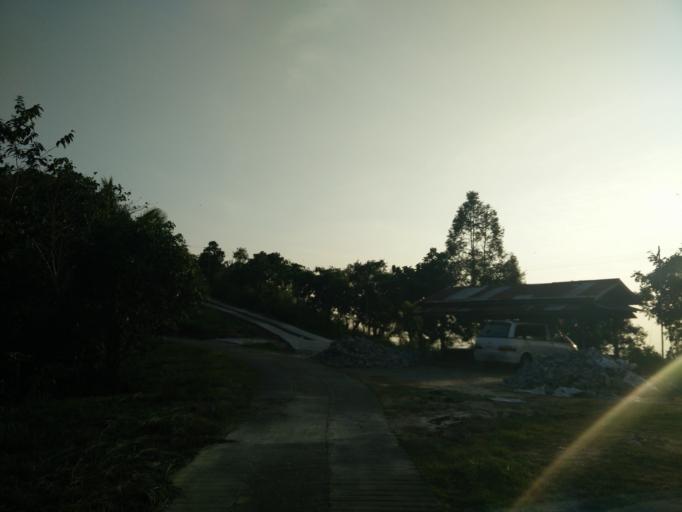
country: MM
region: Mon
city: Thaton
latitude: 16.9270
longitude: 97.3820
